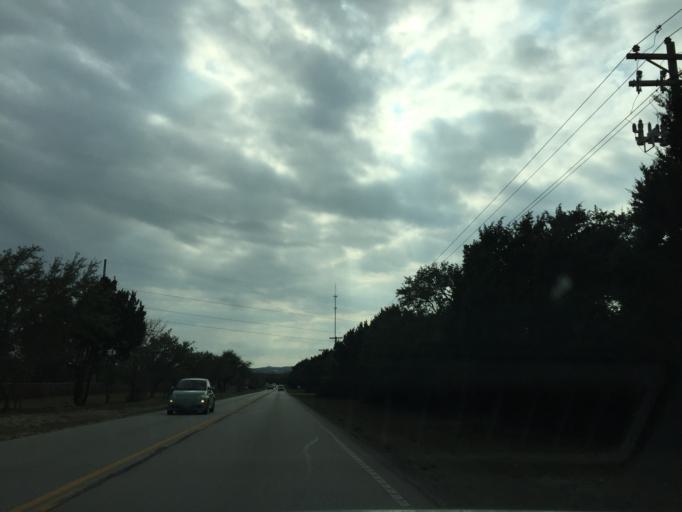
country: US
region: Texas
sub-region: Hays County
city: Dripping Springs
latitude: 30.1391
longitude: -98.0031
